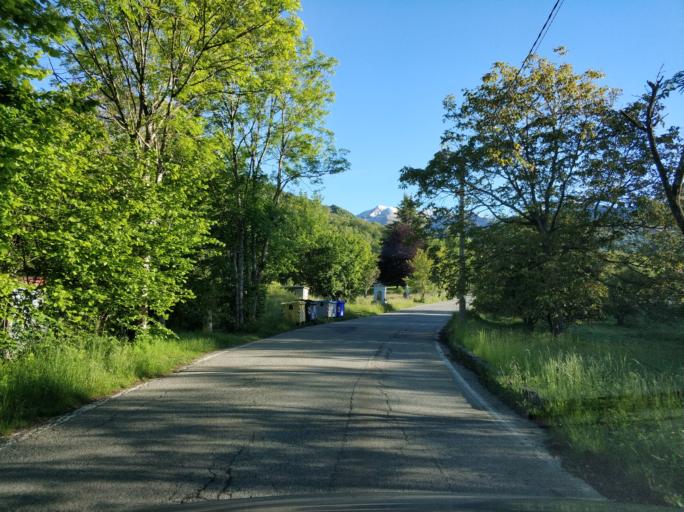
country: IT
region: Piedmont
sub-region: Provincia di Torino
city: Coassolo
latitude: 45.3022
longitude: 7.4669
